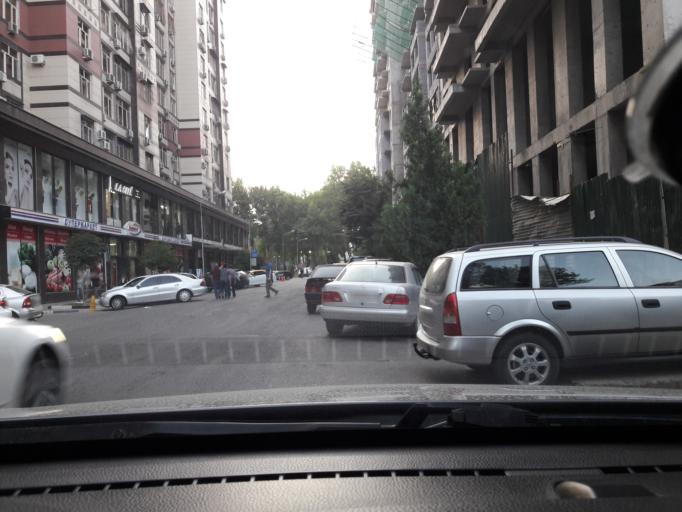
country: TJ
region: Dushanbe
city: Dushanbe
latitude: 38.5681
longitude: 68.7869
